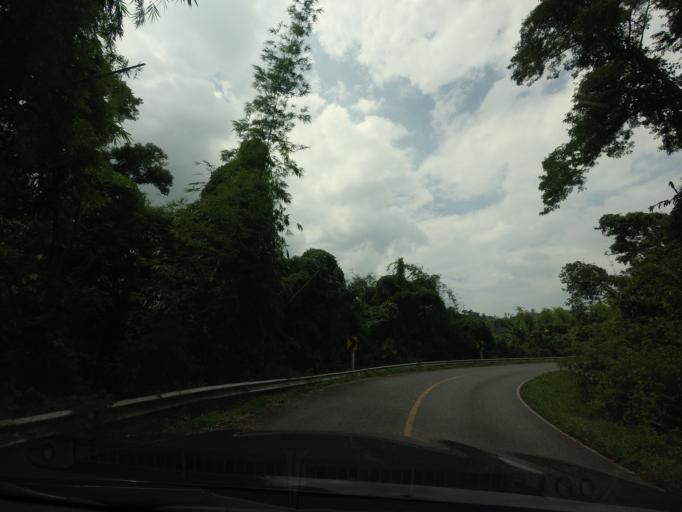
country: TH
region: Loei
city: Na Haeo
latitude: 17.7035
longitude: 100.9480
